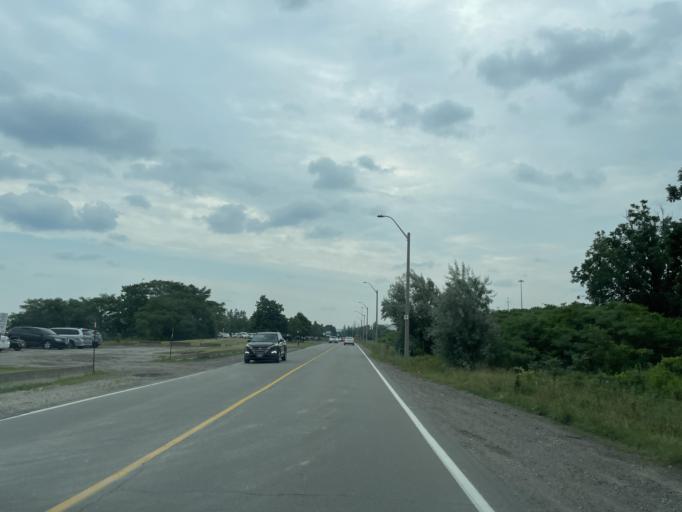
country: CA
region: Ontario
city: Hamilton
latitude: 43.2633
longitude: -79.7706
